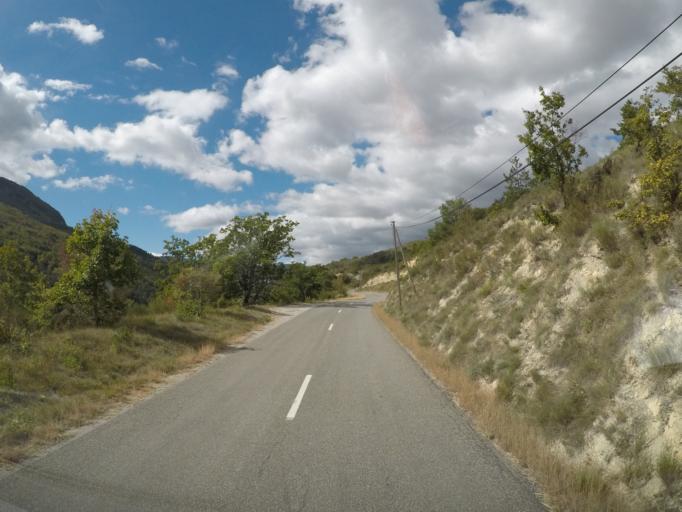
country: FR
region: Provence-Alpes-Cote d'Azur
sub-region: Departement des Hautes-Alpes
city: Laragne-Monteglin
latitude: 44.1776
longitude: 5.6679
